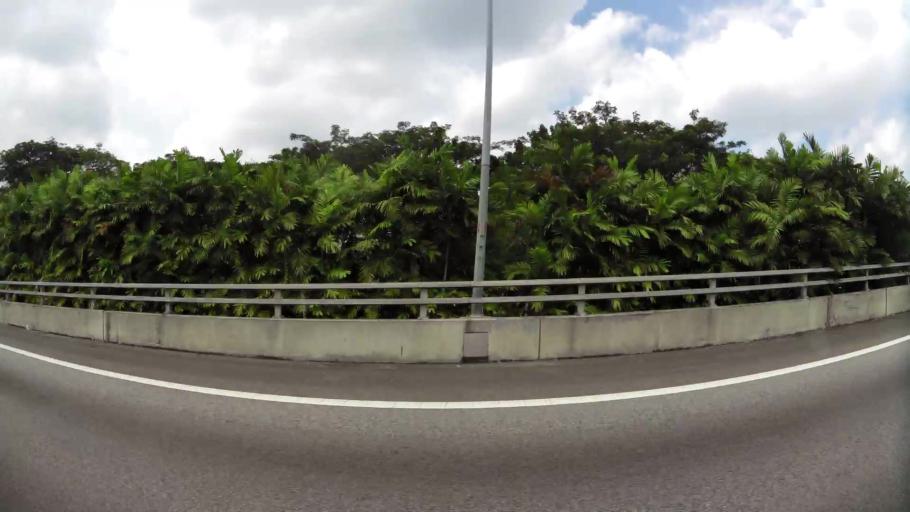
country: SG
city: Singapore
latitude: 1.3615
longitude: 103.9042
